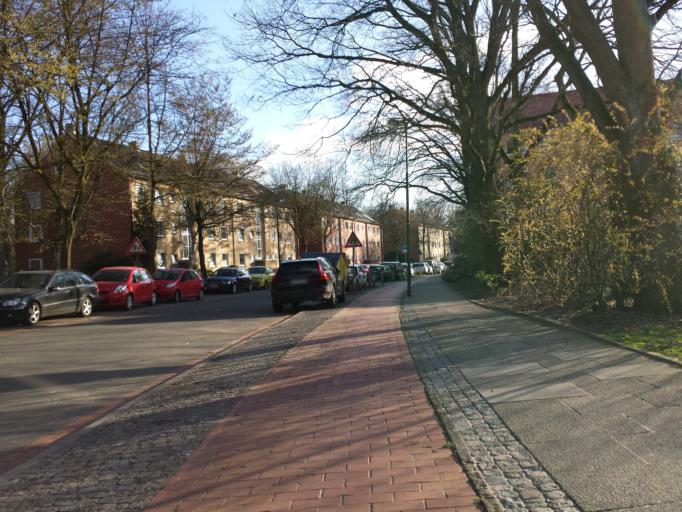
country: DE
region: Bremen
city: Bremen
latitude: 53.0902
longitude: 8.8537
